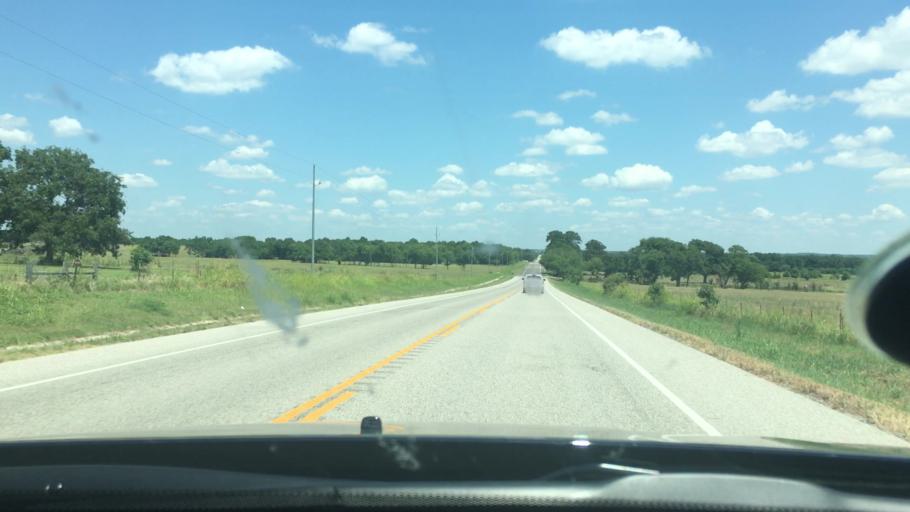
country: US
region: Oklahoma
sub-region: Murray County
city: Sulphur
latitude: 34.3494
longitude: -96.9508
